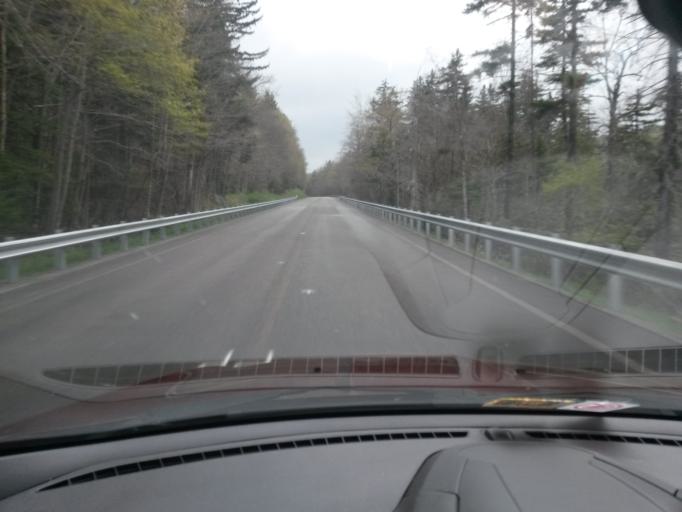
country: US
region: West Virginia
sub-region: Randolph County
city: Elkins
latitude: 38.6258
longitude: -79.8996
